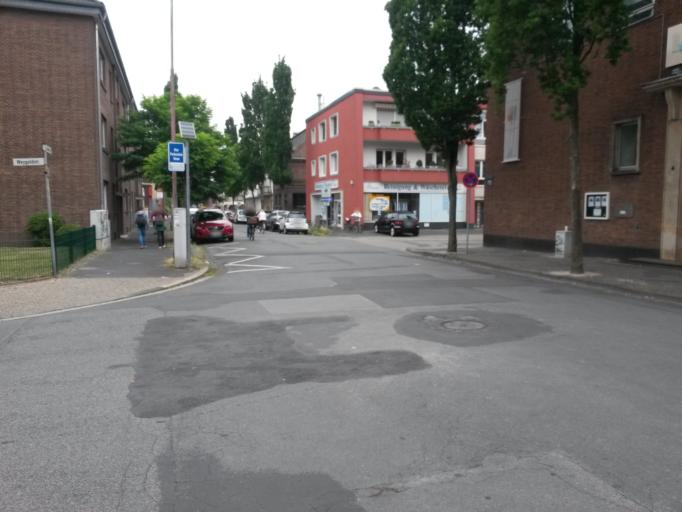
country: DE
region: North Rhine-Westphalia
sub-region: Regierungsbezirk Dusseldorf
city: Moers
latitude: 51.4512
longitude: 6.6326
